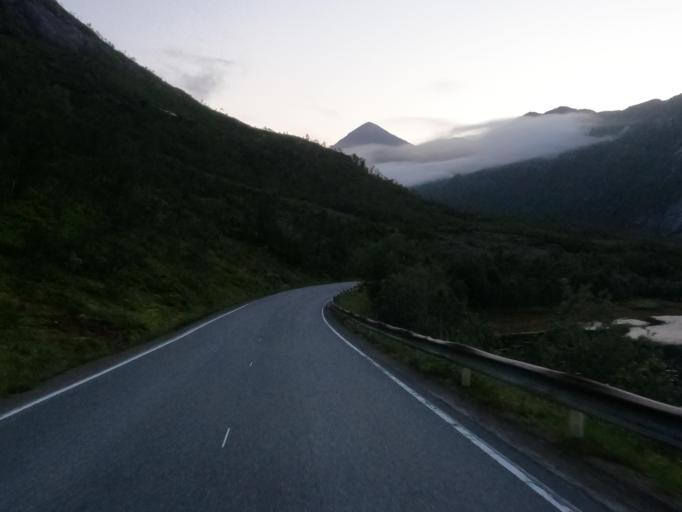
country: NO
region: Nordland
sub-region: Lodingen
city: Lodingen
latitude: 68.5549
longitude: 15.7488
